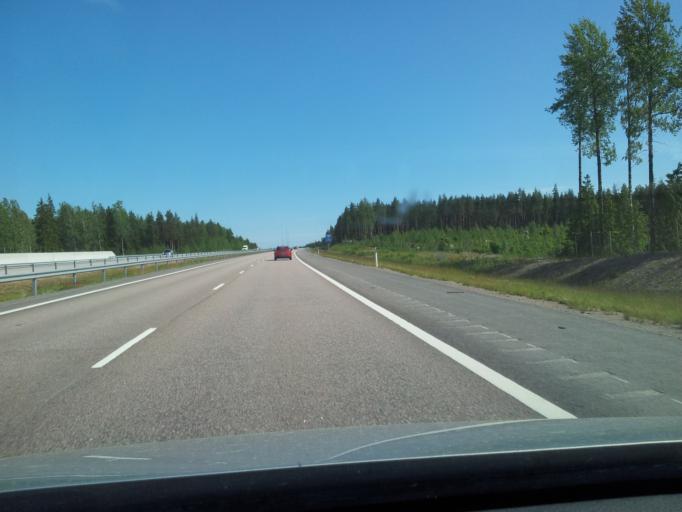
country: FI
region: Uusimaa
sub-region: Loviisa
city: Perna
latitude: 60.4710
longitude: 26.1244
